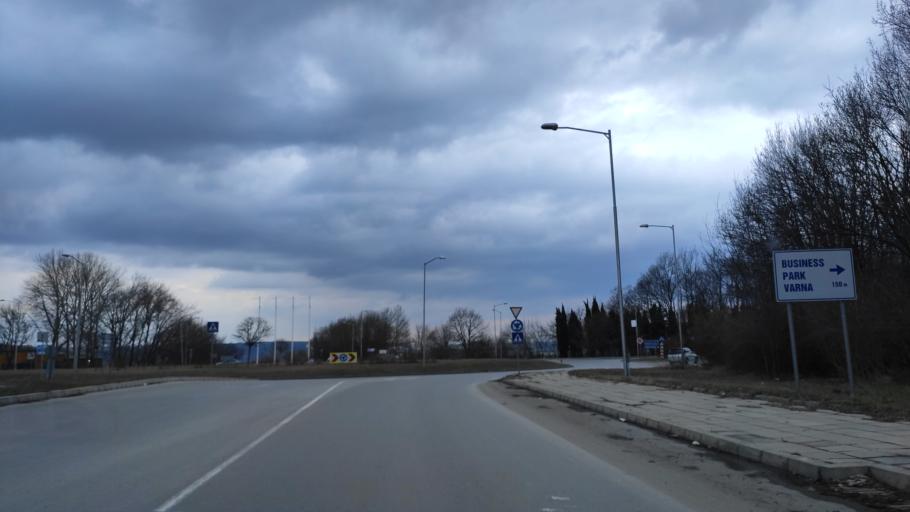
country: BG
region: Varna
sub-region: Obshtina Aksakovo
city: Aksakovo
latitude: 43.2265
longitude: 27.8593
